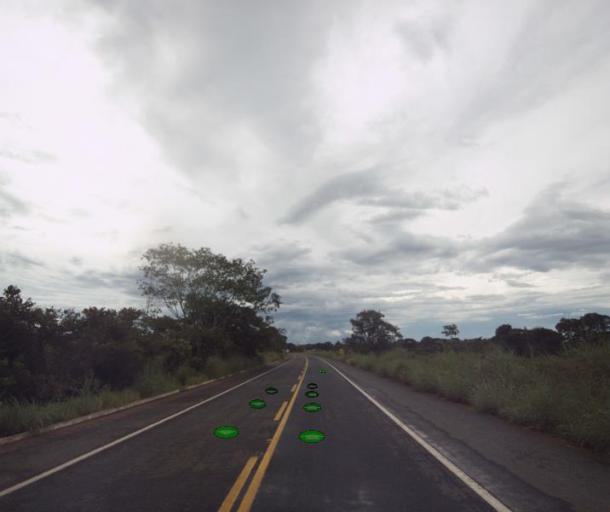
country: BR
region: Goias
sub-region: Sao Miguel Do Araguaia
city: Sao Miguel do Araguaia
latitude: -13.2211
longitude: -50.5721
